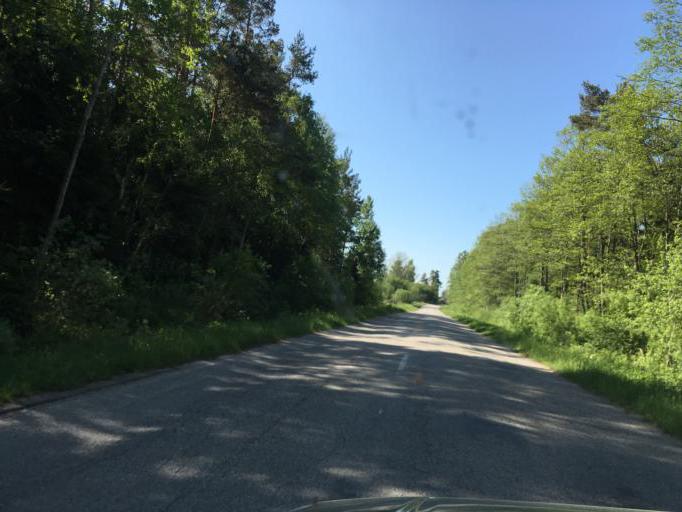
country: LV
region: Ventspils
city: Ventspils
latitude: 57.5065
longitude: 21.8485
